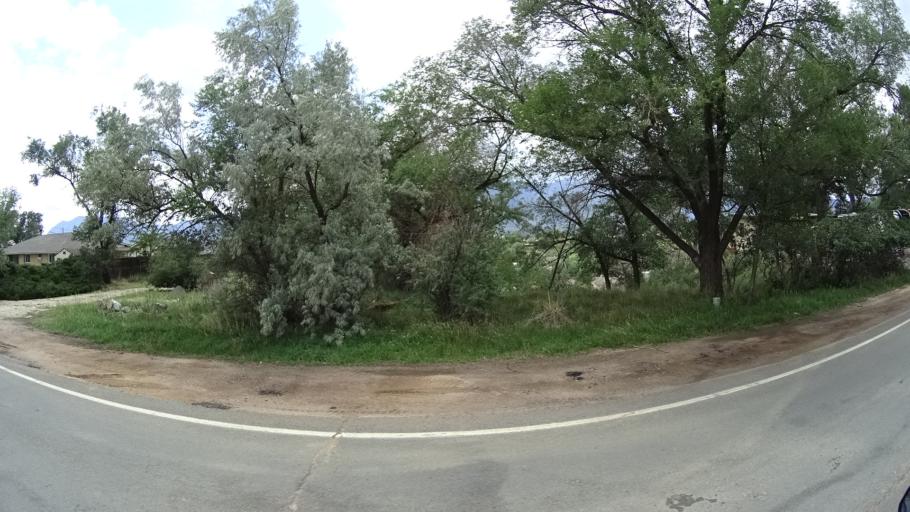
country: US
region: Colorado
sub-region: El Paso County
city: Colorado Springs
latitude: 38.8602
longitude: -104.8487
